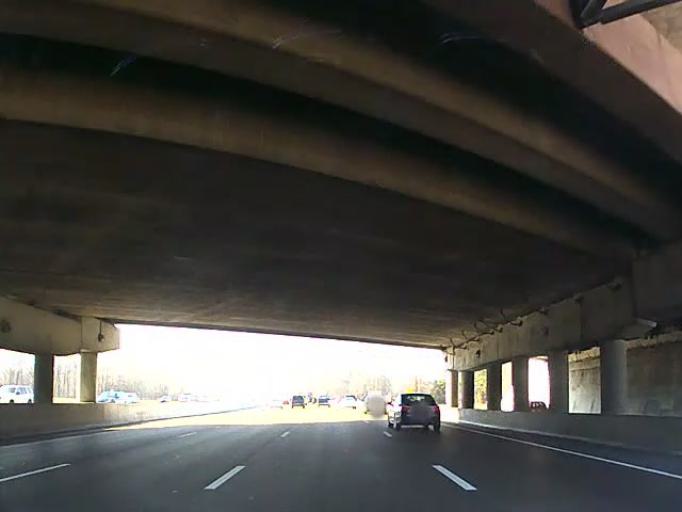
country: US
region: Tennessee
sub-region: Shelby County
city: Germantown
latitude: 35.0832
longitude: -89.8945
